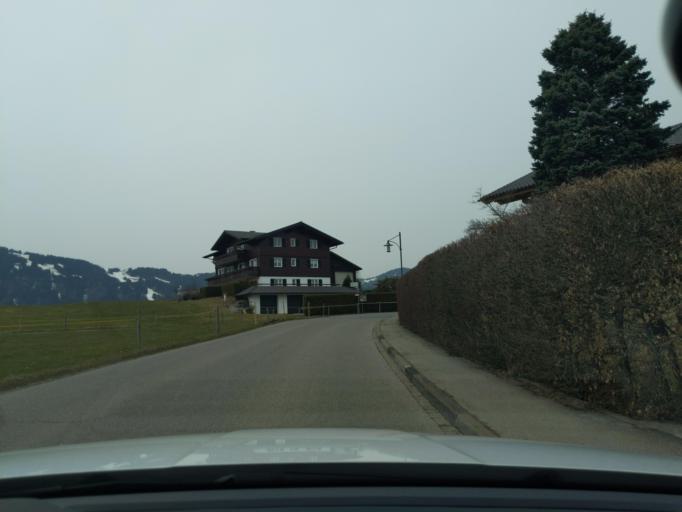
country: DE
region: Bavaria
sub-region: Swabia
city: Ofterschwang
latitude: 47.4862
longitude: 10.2637
